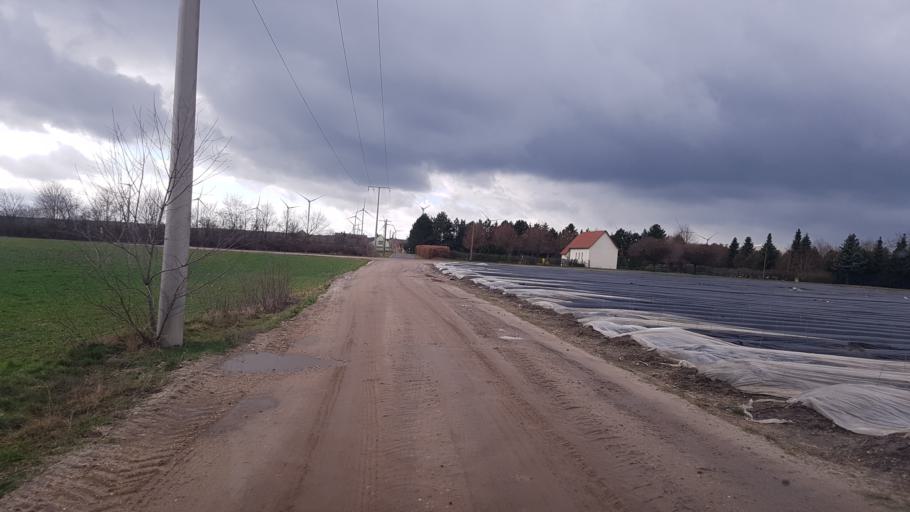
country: DE
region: Brandenburg
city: Bronkow
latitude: 51.6403
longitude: 13.8690
